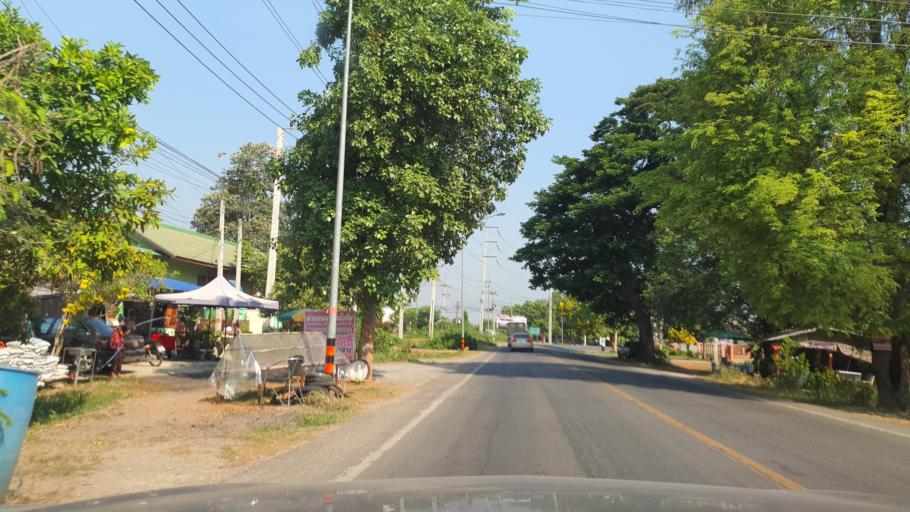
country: TH
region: Kanchanaburi
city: Kanchanaburi
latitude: 14.0442
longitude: 99.4724
